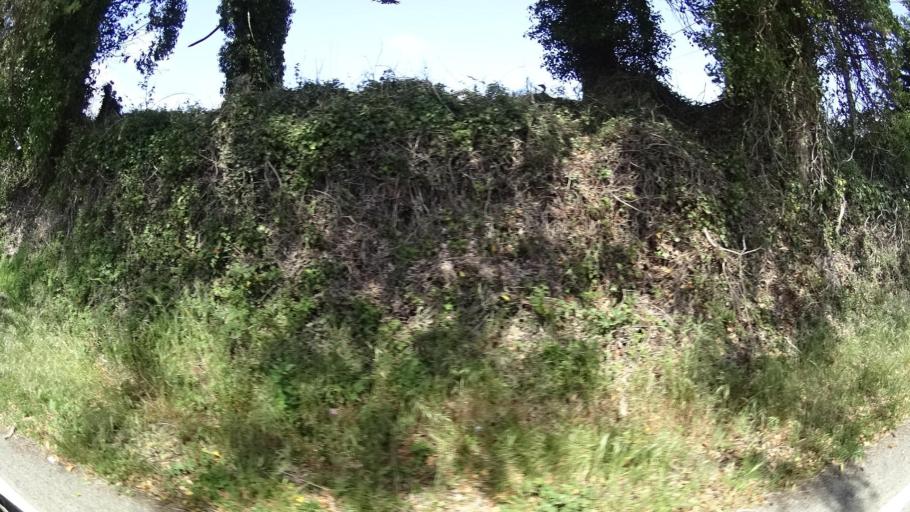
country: US
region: California
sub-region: Humboldt County
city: Humboldt Hill
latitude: 40.6549
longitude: -124.2174
